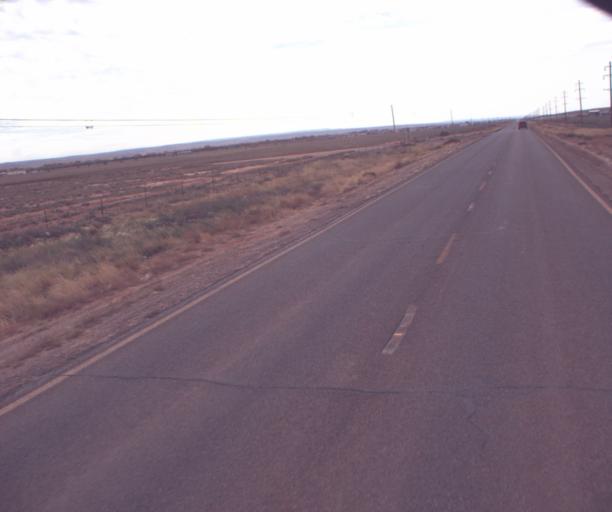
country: US
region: Arizona
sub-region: Apache County
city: Chinle
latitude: 36.2059
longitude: -109.5995
